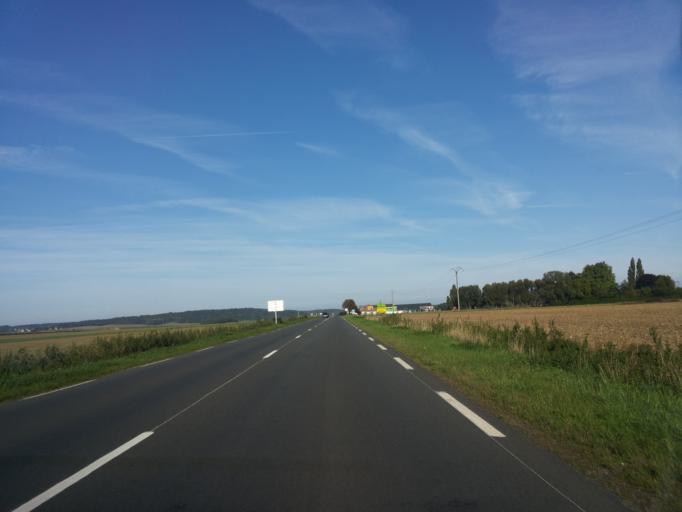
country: FR
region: Picardie
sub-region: Departement de l'Aisne
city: Aulnois-sous-Laon
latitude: 49.5826
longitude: 3.5697
